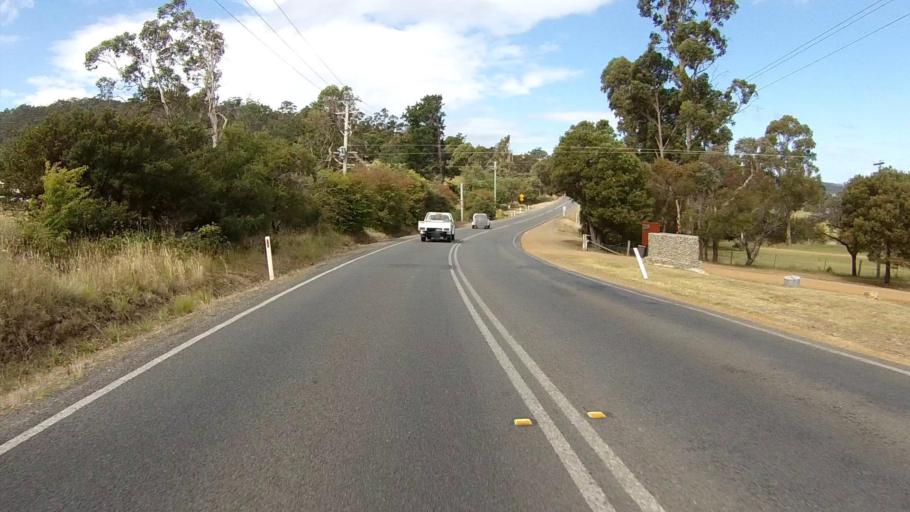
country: AU
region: Tasmania
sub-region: Clarence
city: Rokeby
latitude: -42.9069
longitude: 147.4602
